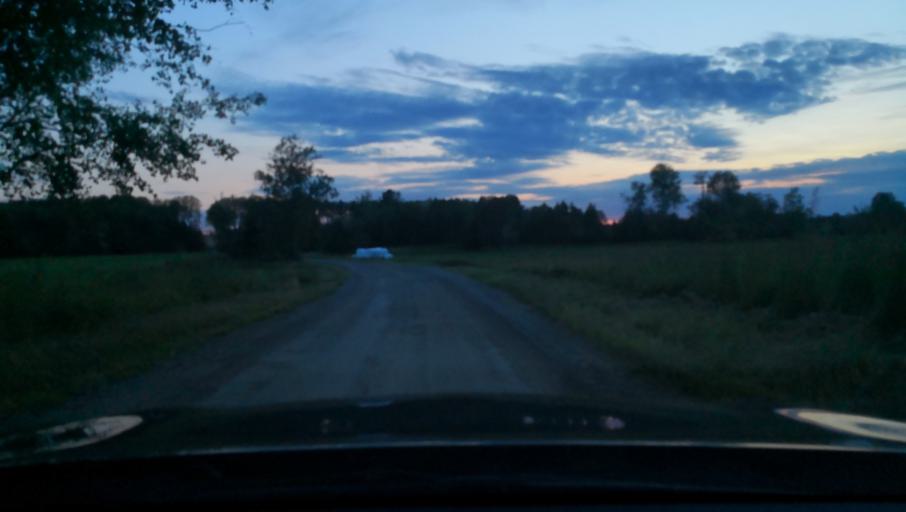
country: SE
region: Uppsala
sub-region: Osthammars Kommun
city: Bjorklinge
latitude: 60.0030
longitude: 17.3514
